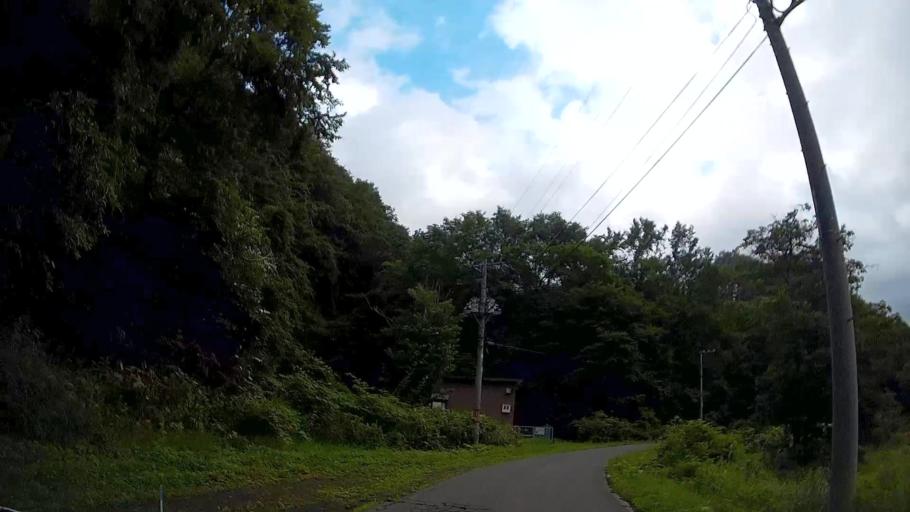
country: JP
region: Hokkaido
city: Nanae
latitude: 42.0761
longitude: 140.5256
